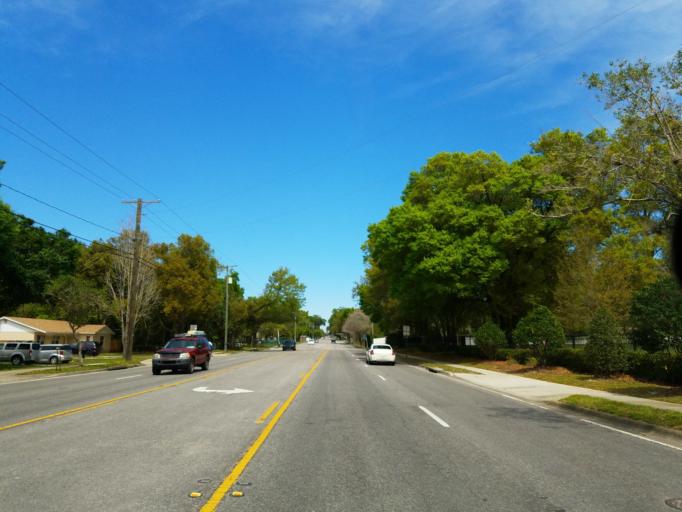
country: US
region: Florida
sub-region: Hillsborough County
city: Seffner
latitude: 27.9656
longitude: -82.2858
